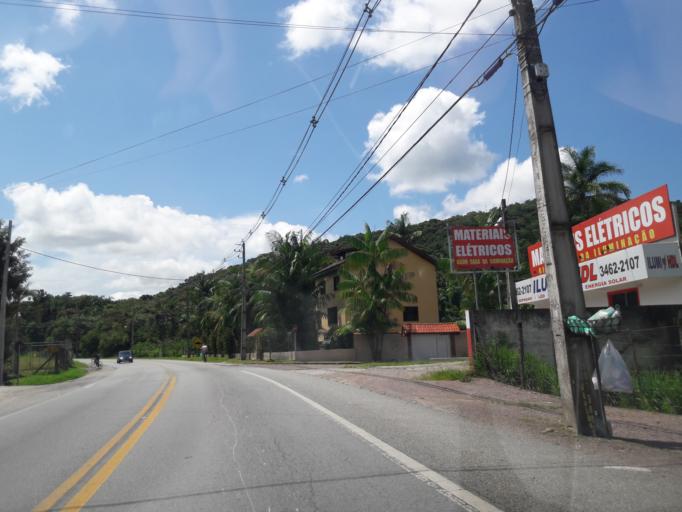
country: BR
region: Parana
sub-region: Antonina
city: Antonina
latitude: -25.4760
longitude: -48.8291
